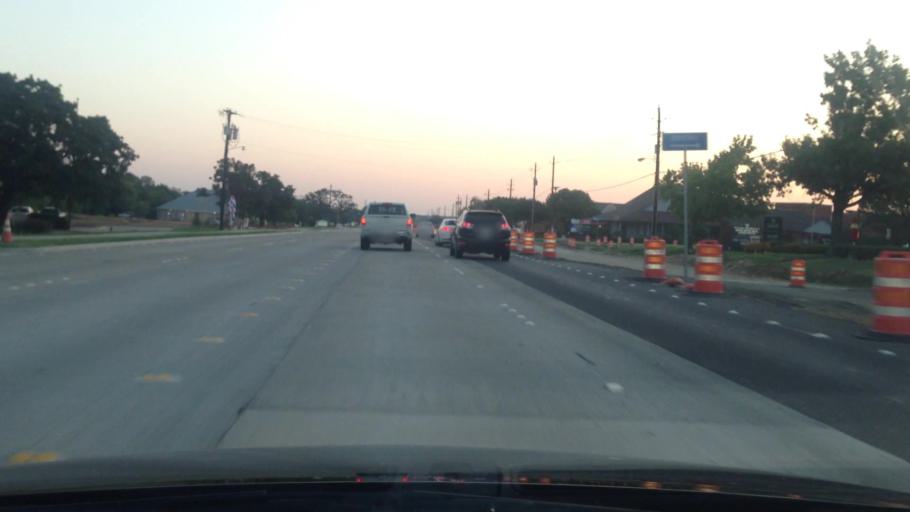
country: US
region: Texas
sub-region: Tarrant County
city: Colleyville
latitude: 32.9014
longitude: -97.1420
